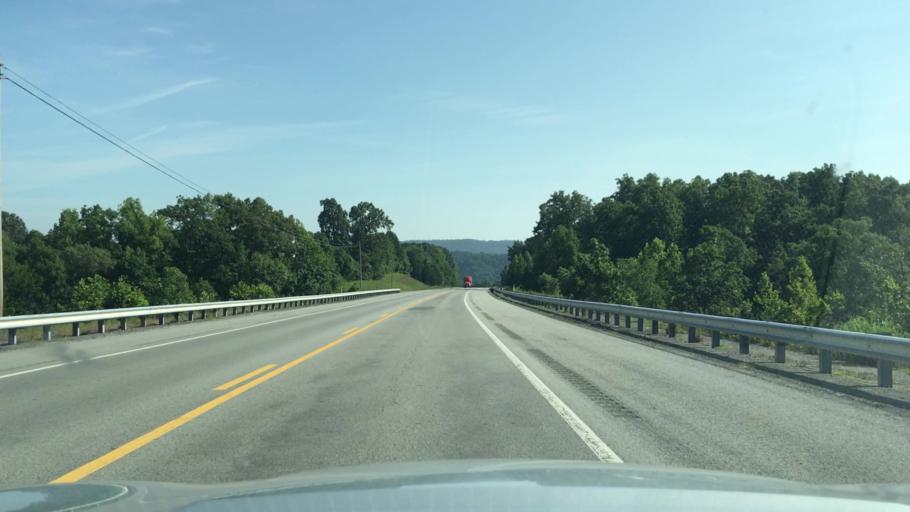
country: US
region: Tennessee
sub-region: Pickett County
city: Byrdstown
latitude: 36.5199
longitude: -85.1678
